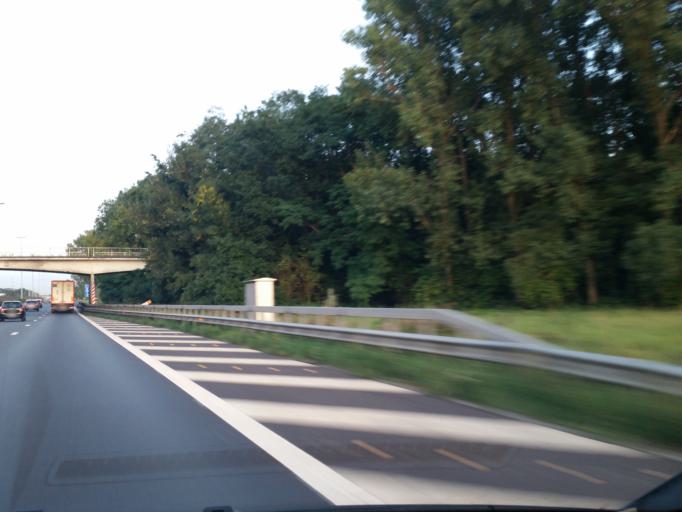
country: BE
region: Flanders
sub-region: Provincie Oost-Vlaanderen
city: Nevele
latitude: 51.0621
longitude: 3.5114
